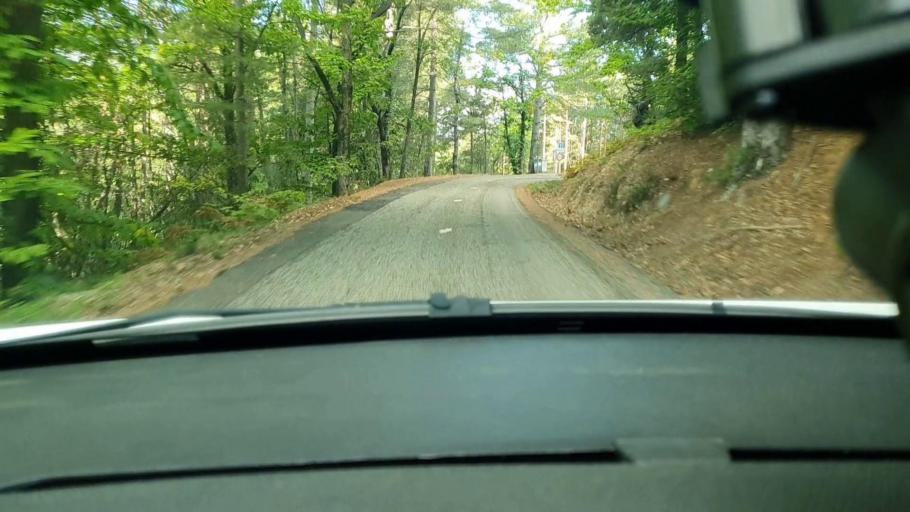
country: FR
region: Rhone-Alpes
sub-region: Departement de l'Ardeche
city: Les Vans
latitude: 44.4075
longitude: 4.0070
